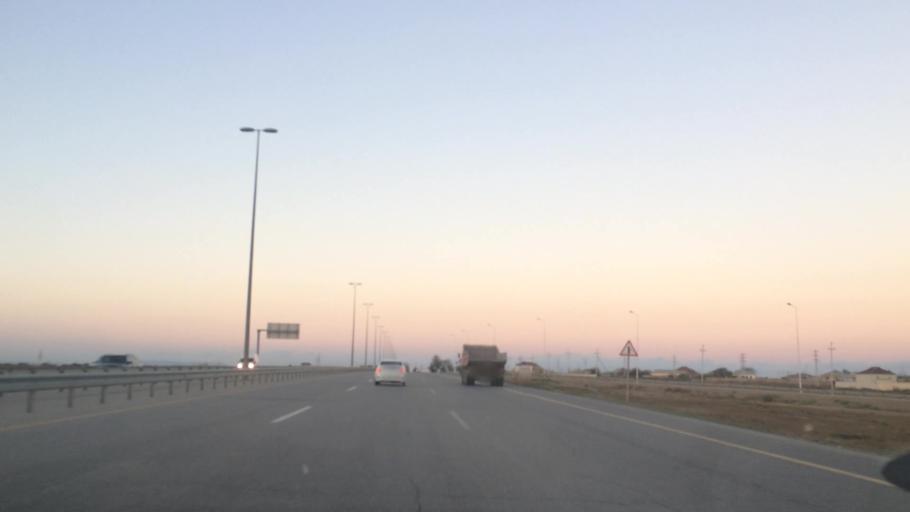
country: AZ
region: Baki
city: Qobustan
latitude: 39.9826
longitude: 49.4242
